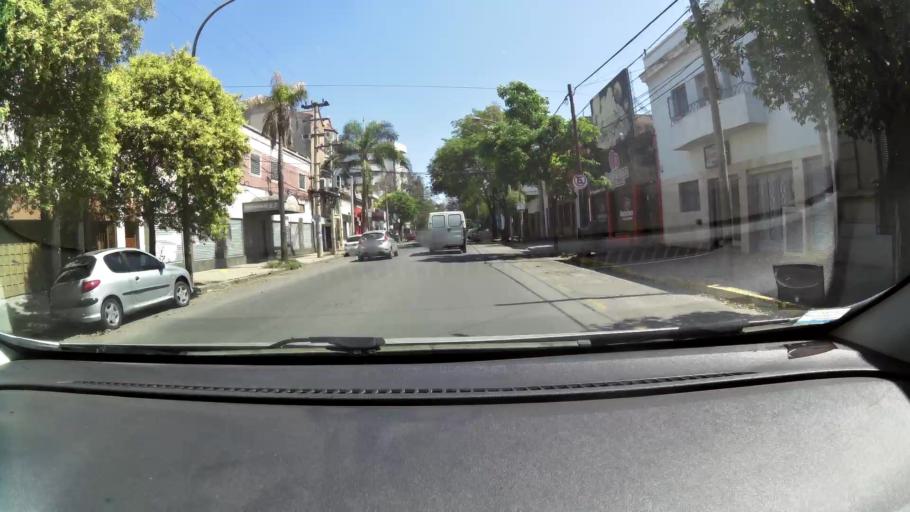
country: AR
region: Cordoba
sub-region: Departamento de Capital
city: Cordoba
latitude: -31.3949
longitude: -64.1855
